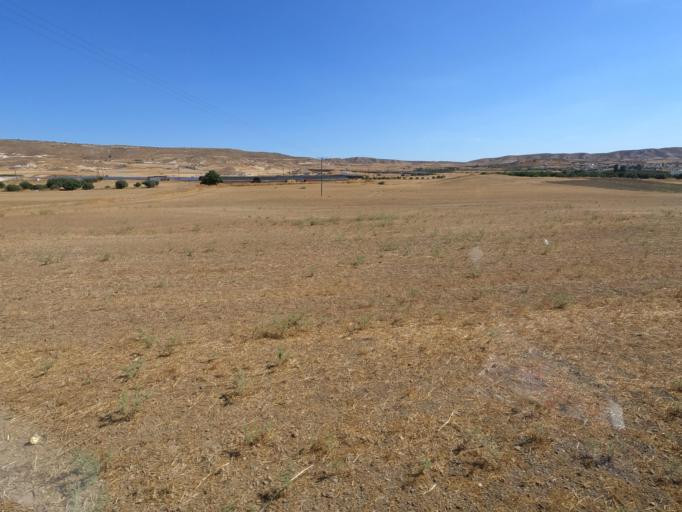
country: CY
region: Larnaka
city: Troulloi
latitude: 35.0250
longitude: 33.5978
